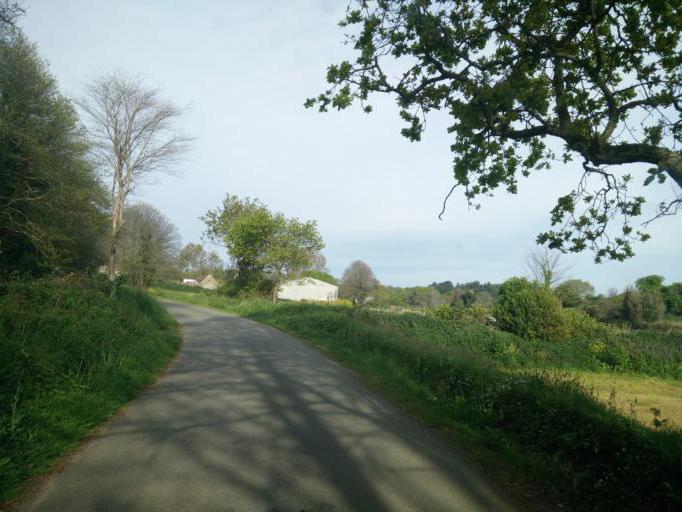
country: FR
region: Brittany
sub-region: Departement des Cotes-d'Armor
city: Lezardrieux
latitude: 48.8300
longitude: -3.0820
